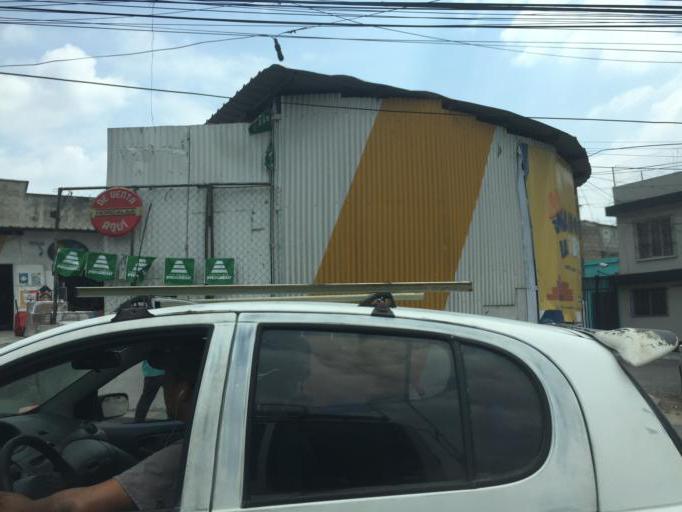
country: GT
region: Guatemala
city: Petapa
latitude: 14.5269
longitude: -90.5530
